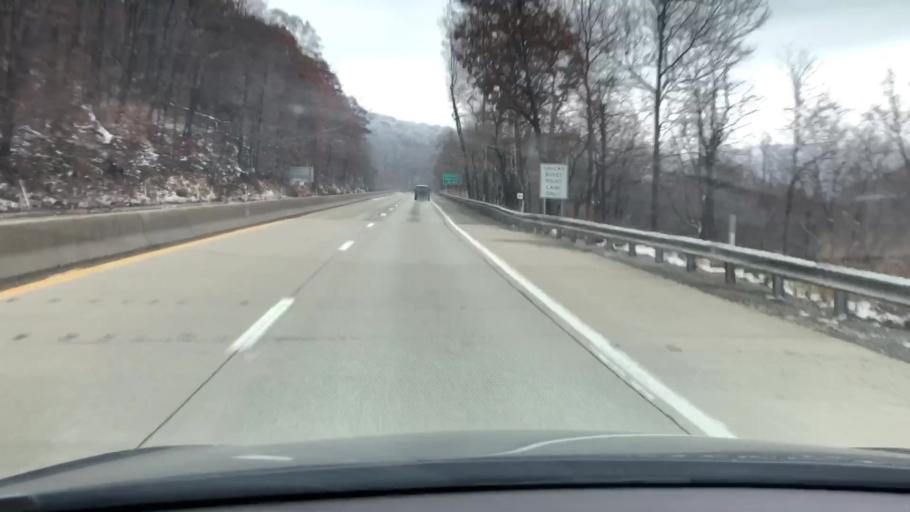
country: US
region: Pennsylvania
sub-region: Fayette County
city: Hopwood
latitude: 39.8669
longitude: -79.6876
